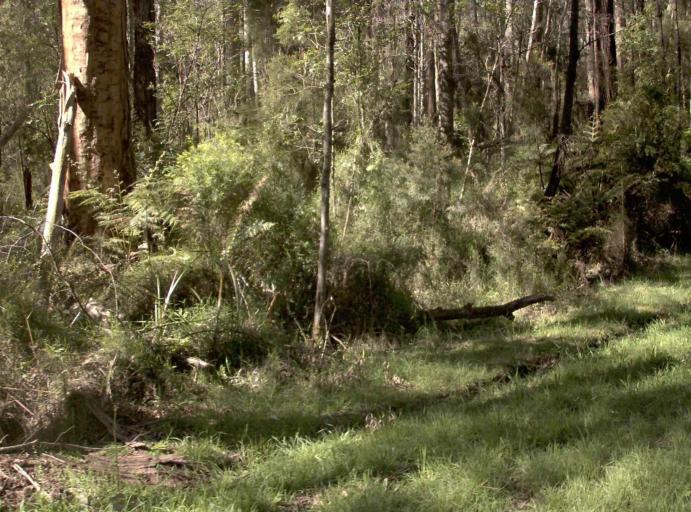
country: AU
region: Victoria
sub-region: Baw Baw
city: Warragul
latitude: -37.8896
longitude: 145.9099
